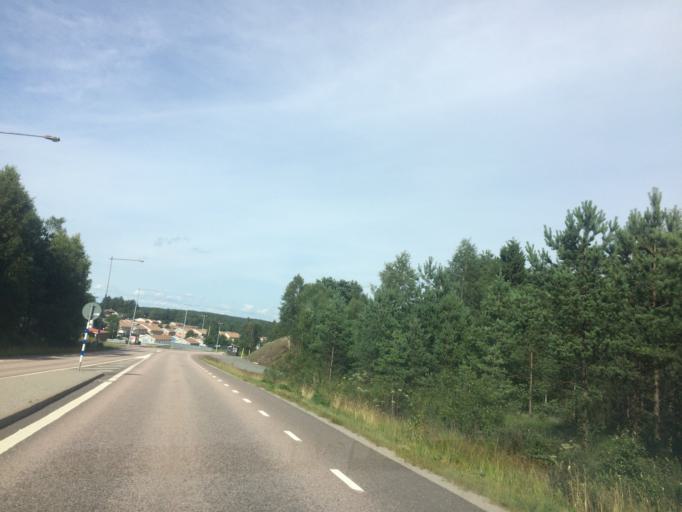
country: SE
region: Vaestra Goetaland
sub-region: Partille Kommun
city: Furulund
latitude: 57.7008
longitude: 12.1444
